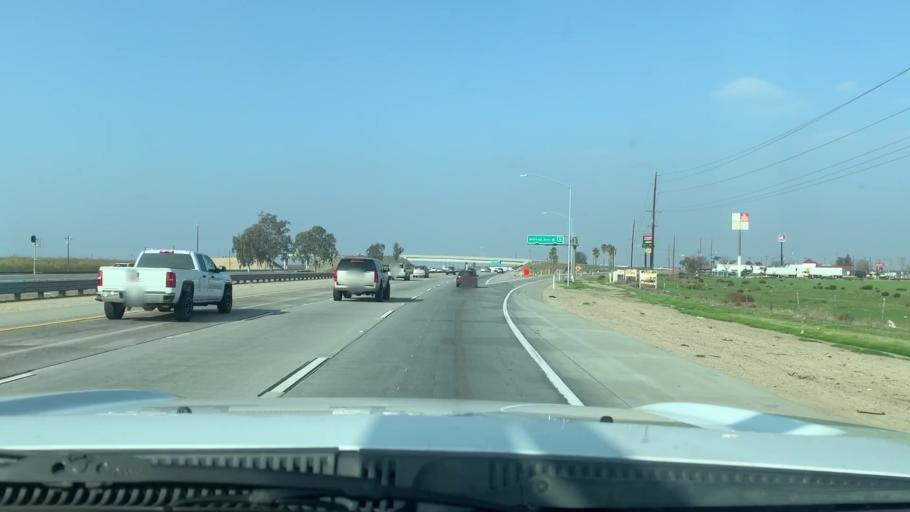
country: US
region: California
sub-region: Kern County
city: Shafter
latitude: 35.5258
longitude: -119.1882
